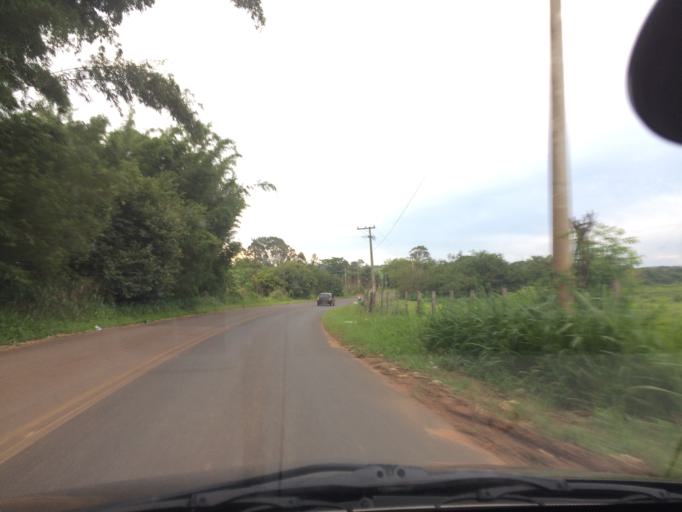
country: BR
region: Sao Paulo
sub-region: Casa Branca
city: Casa Branca
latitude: -21.7676
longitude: -47.1000
